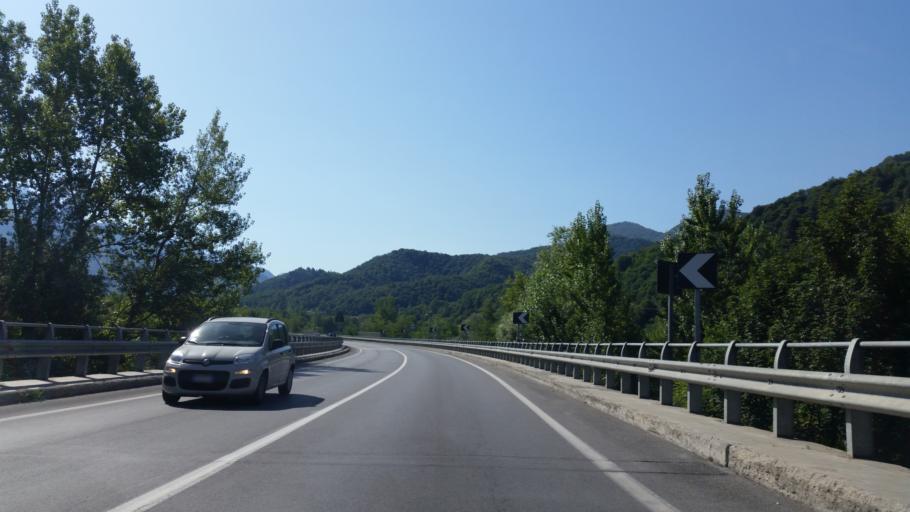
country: IT
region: Piedmont
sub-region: Provincia di Cuneo
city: Roccavione
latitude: 44.3158
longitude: 7.4876
